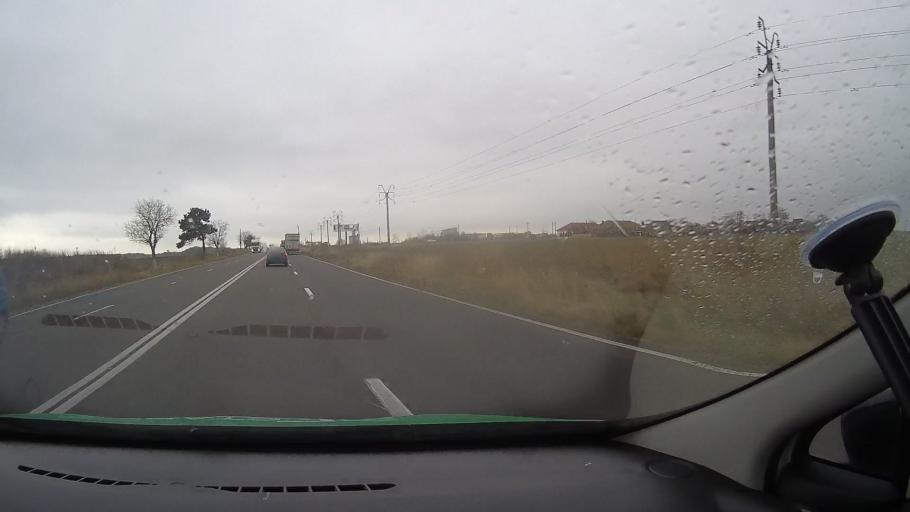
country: RO
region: Constanta
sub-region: Comuna Valu lui Traian
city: Valu lui Traian
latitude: 44.1657
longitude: 28.5251
